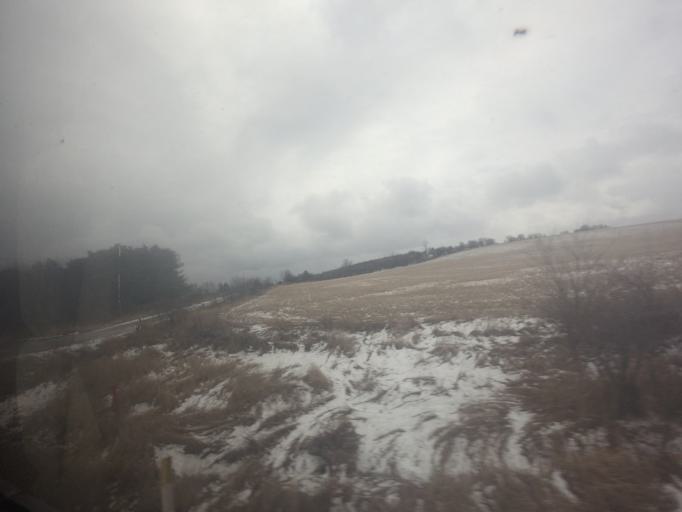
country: CA
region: Ontario
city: Cobourg
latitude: 43.9459
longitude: -78.3498
